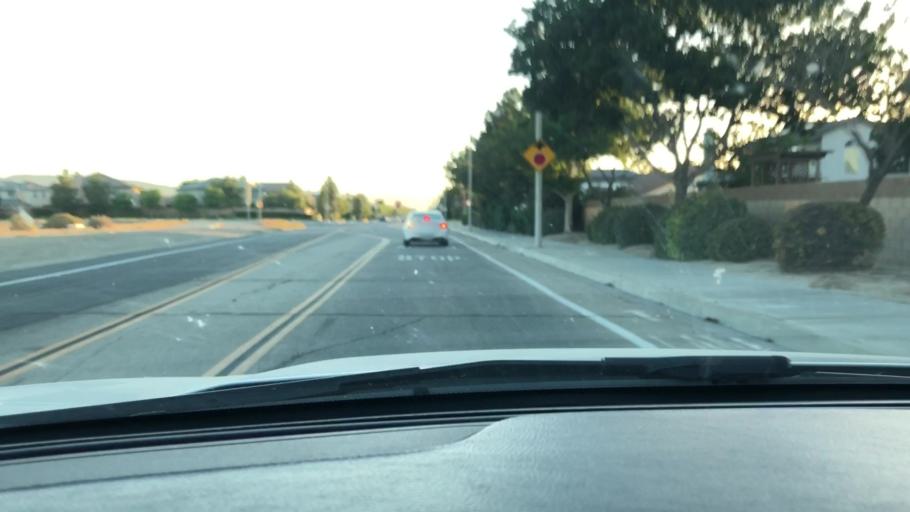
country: US
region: California
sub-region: Los Angeles County
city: Quartz Hill
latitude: 34.6821
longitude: -118.2001
